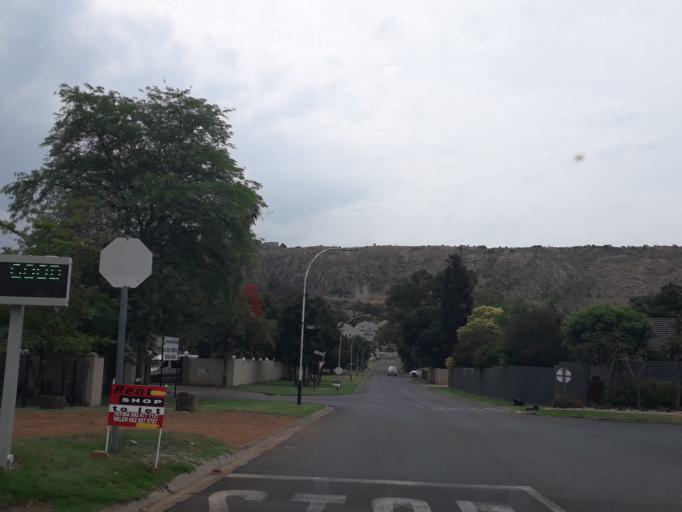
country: ZA
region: Gauteng
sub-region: City of Johannesburg Metropolitan Municipality
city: Johannesburg
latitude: -26.1754
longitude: 28.1162
